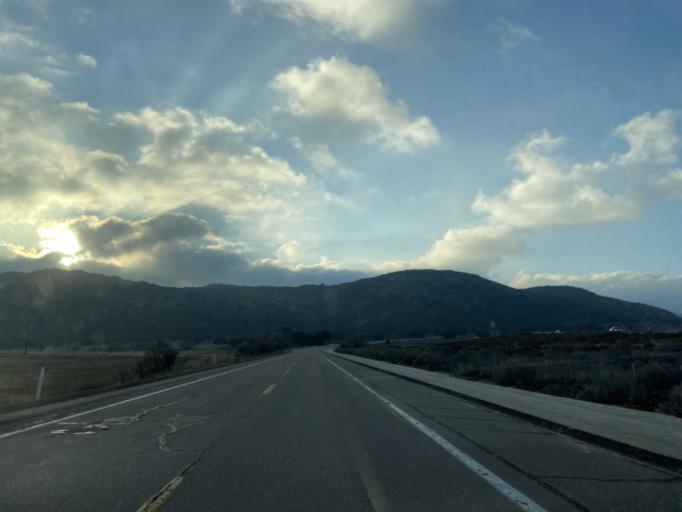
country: US
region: California
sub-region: San Diego County
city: Campo
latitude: 32.7173
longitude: -116.4664
